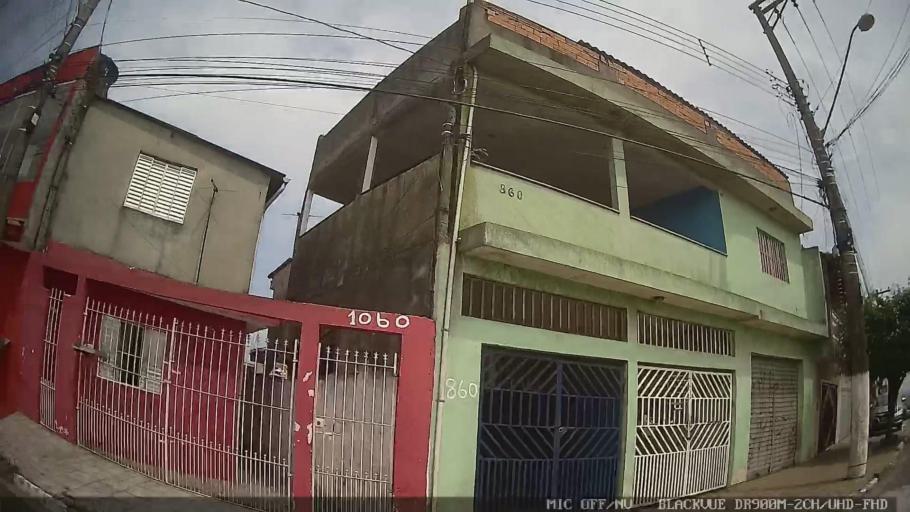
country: BR
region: Sao Paulo
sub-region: Ferraz De Vasconcelos
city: Ferraz de Vasconcelos
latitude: -23.5247
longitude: -46.3627
